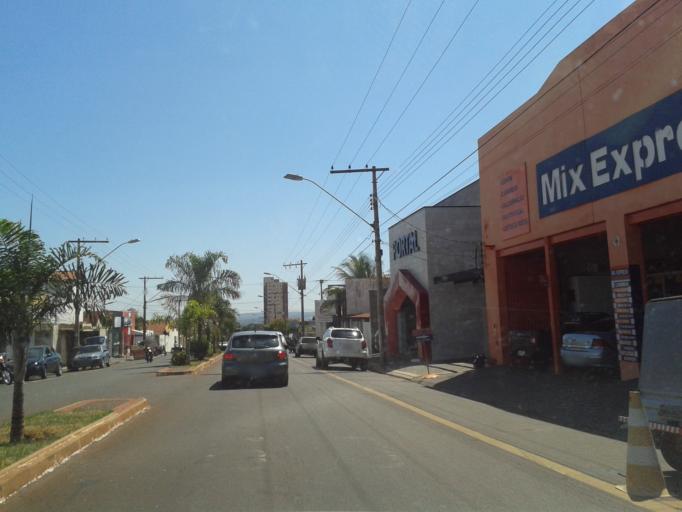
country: BR
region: Minas Gerais
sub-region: Ituiutaba
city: Ituiutaba
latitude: -18.9798
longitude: -49.4587
